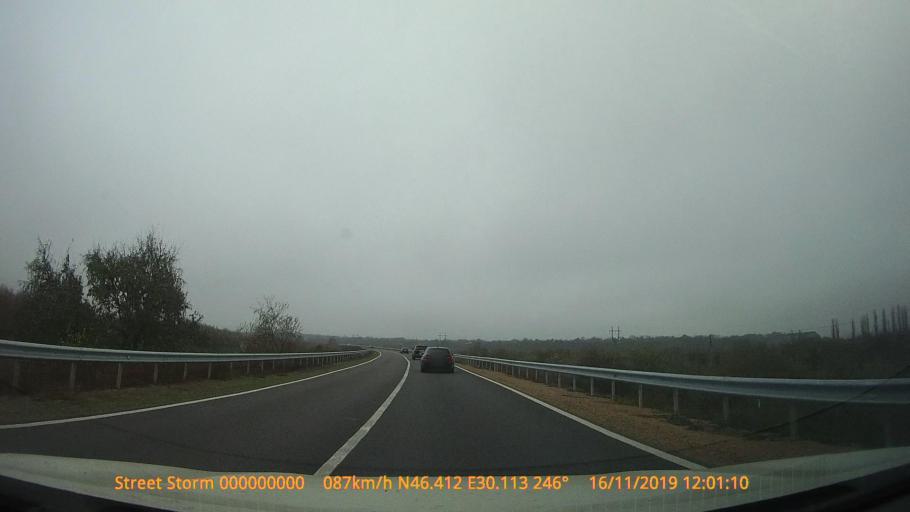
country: UA
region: Odessa
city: Bilyayivka
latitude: 46.4112
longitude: 30.1104
